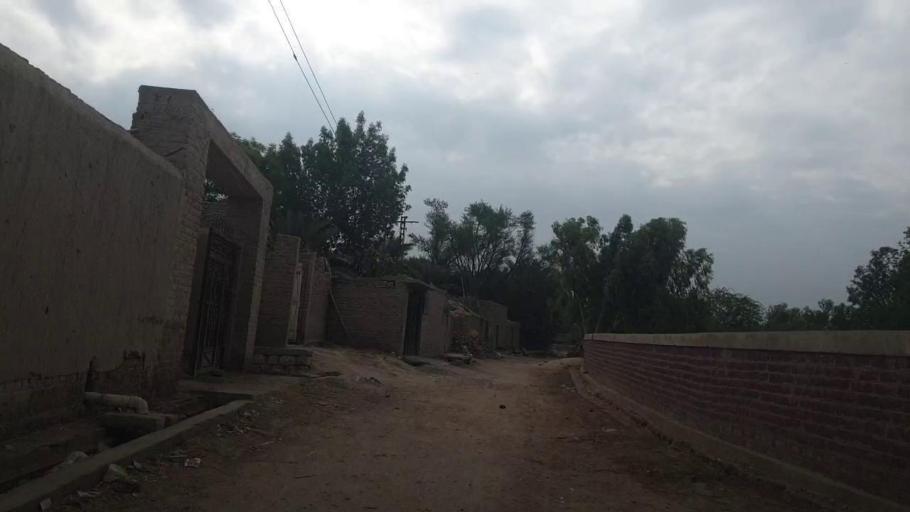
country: PK
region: Sindh
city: Sukkur
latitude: 27.6363
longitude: 68.7925
